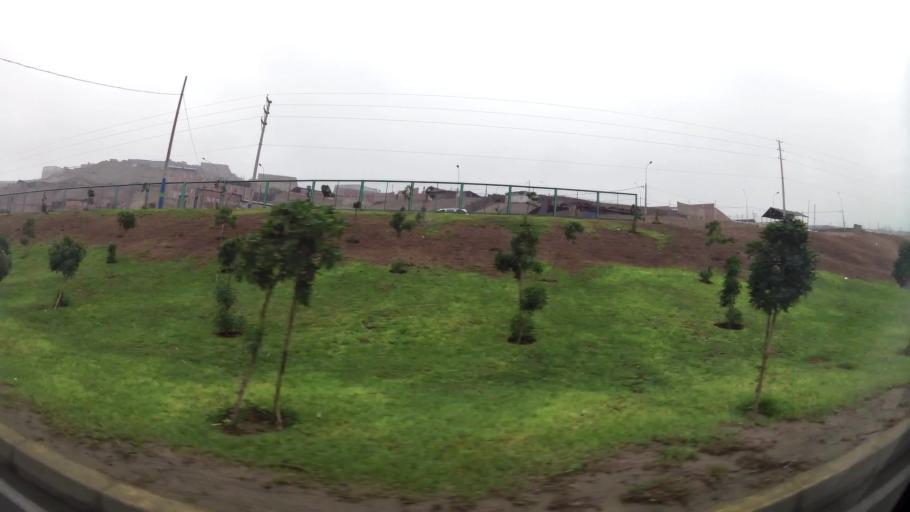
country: PE
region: Lima
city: Ventanilla
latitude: -11.8539
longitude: -77.1296
